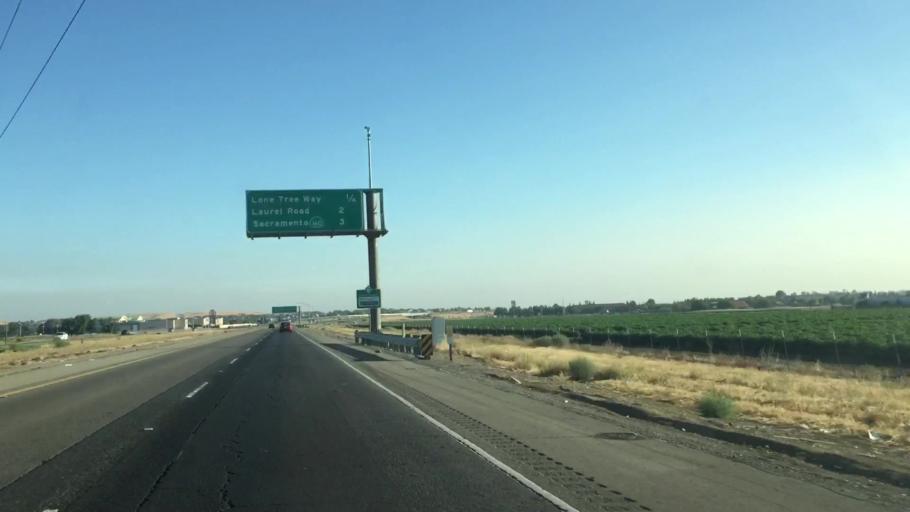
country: US
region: California
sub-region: Contra Costa County
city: Brentwood
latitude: 37.9515
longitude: -121.7444
